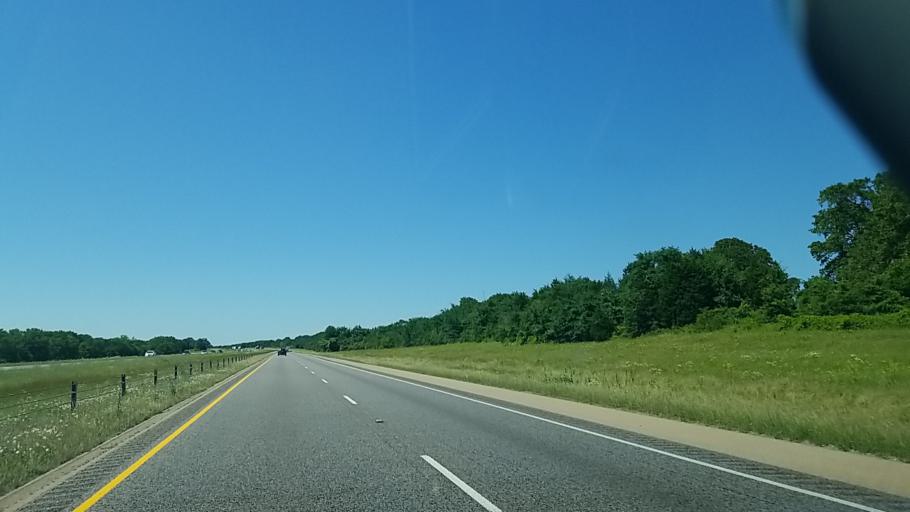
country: US
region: Texas
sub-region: Freestone County
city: Fairfield
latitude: 31.6806
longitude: -96.1648
